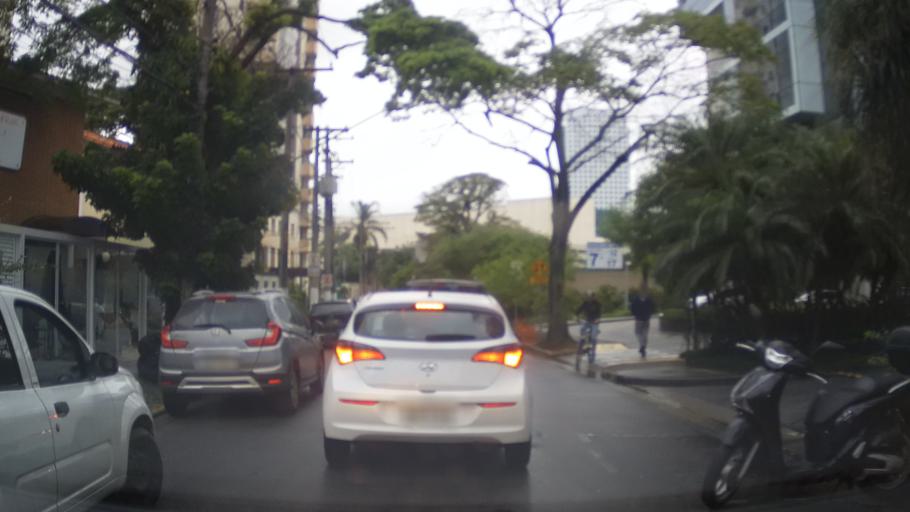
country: BR
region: Sao Paulo
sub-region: Sao Paulo
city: Sao Paulo
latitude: -23.5700
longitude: -46.6918
